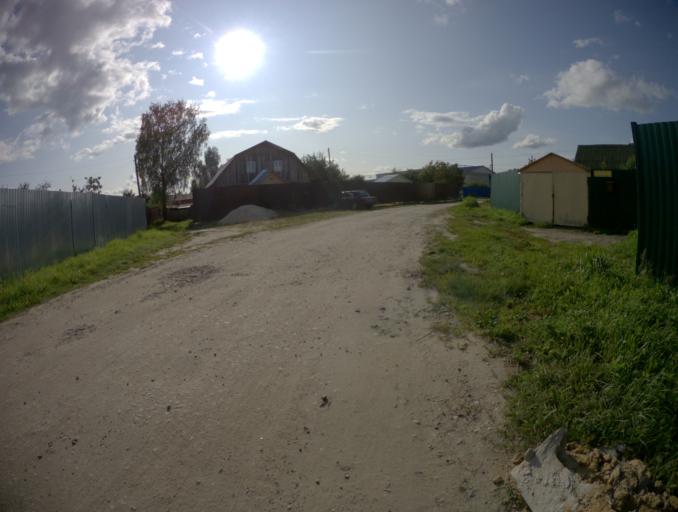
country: RU
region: Vladimir
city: Lakinsk
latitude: 56.0194
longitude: 39.9848
